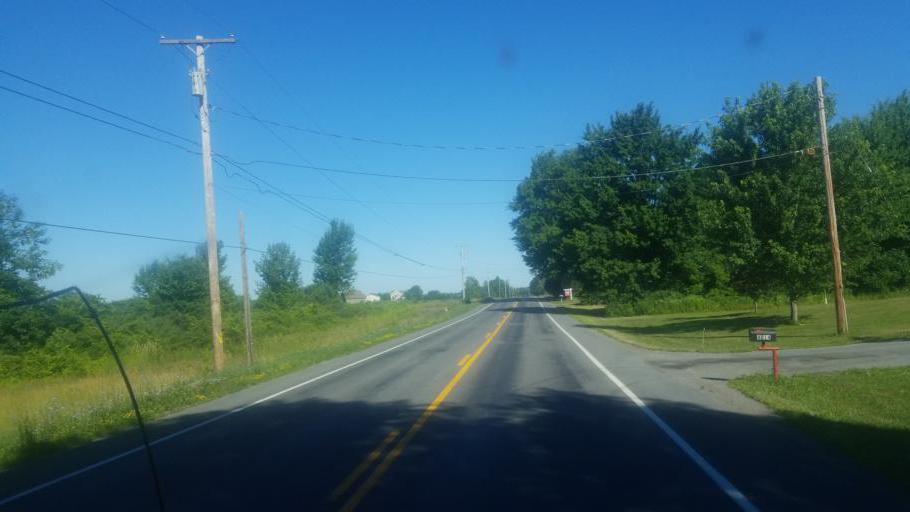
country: US
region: New York
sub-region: Ontario County
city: Canandaigua
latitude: 42.8391
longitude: -77.2199
